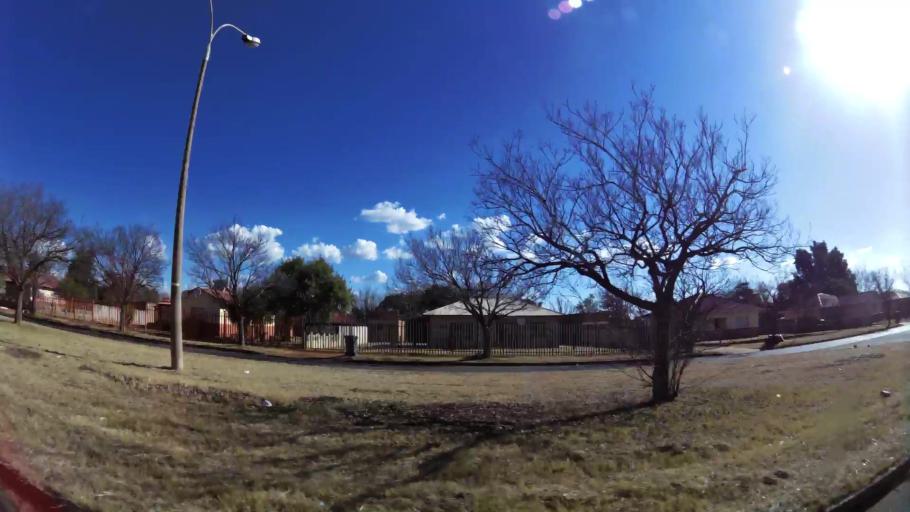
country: ZA
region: Gauteng
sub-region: West Rand District Municipality
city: Carletonville
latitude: -26.3664
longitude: 27.3942
